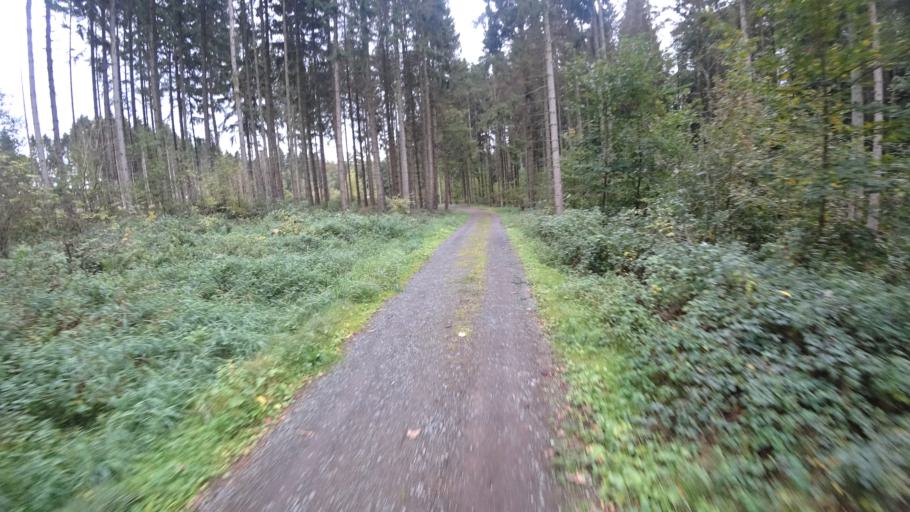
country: DE
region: Rheinland-Pfalz
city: Nordhofen
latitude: 50.5271
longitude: 7.7348
